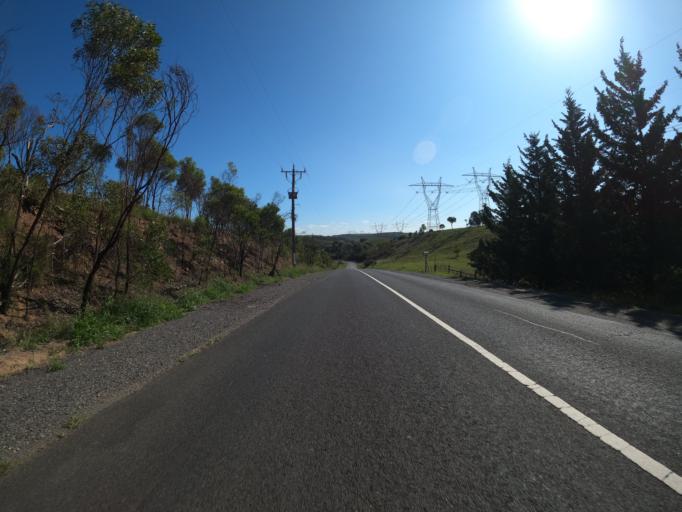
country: AU
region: Victoria
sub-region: Hume
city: Greenvale
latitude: -37.5532
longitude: 144.8543
